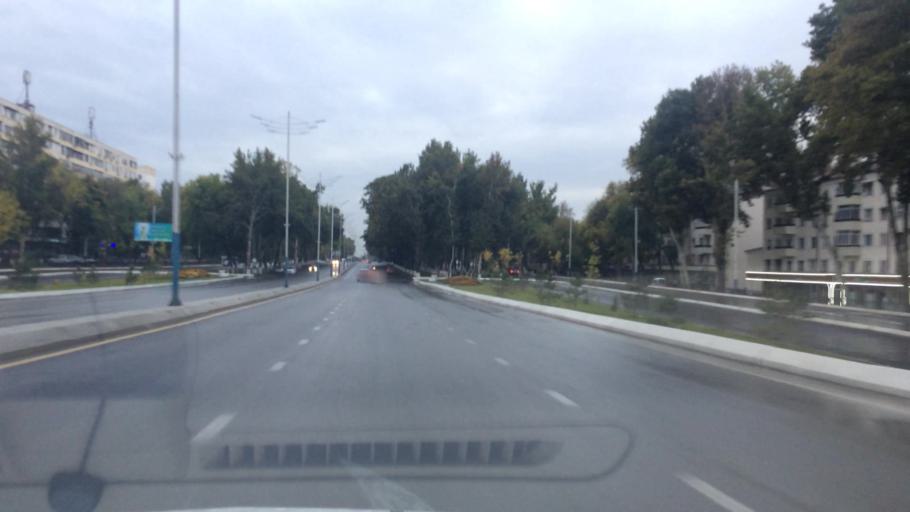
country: UZ
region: Toshkent Shahri
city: Tashkent
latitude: 41.2901
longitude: 69.2211
